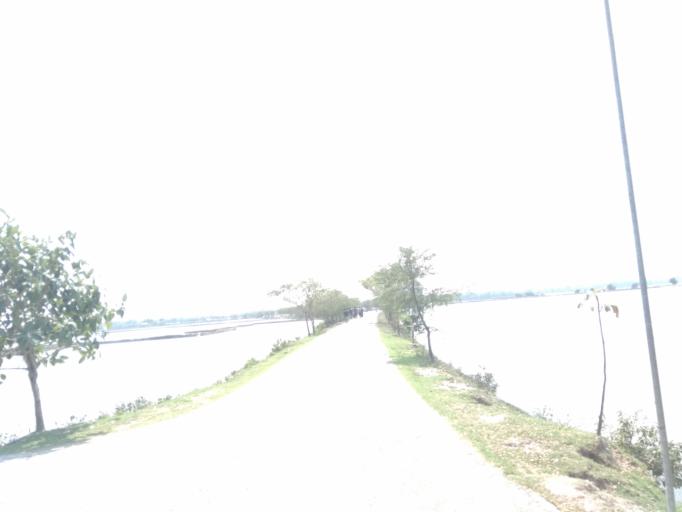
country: IN
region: West Bengal
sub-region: North 24 Parganas
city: Taki
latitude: 22.4009
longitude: 89.2140
